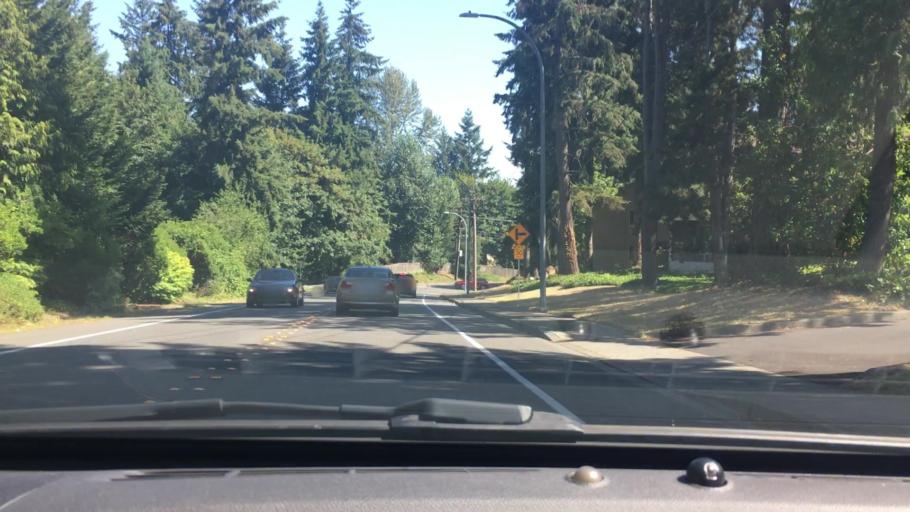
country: US
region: Washington
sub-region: King County
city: Sammamish
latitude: 47.6177
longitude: -122.1083
